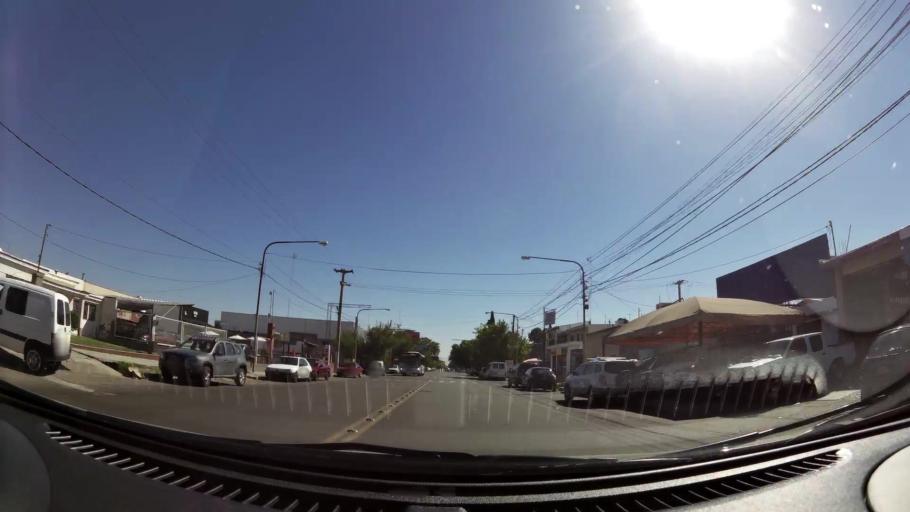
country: AR
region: Mendoza
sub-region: Departamento de Maipu
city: Maipu
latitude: -32.9614
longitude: -68.7903
